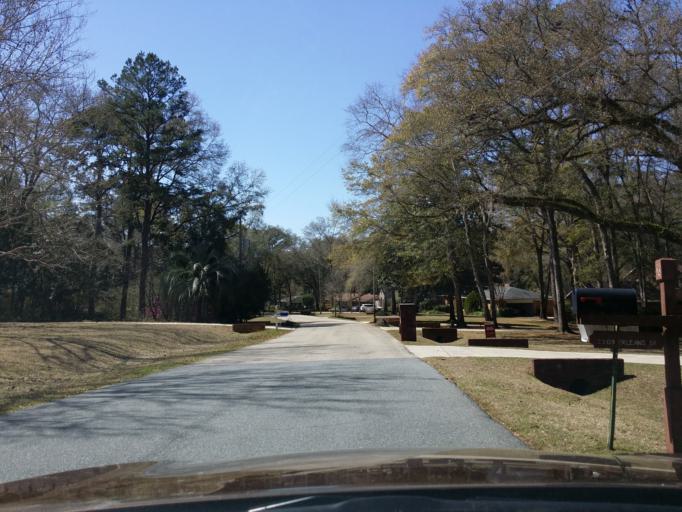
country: US
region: Florida
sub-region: Leon County
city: Tallahassee
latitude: 30.4870
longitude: -84.1863
